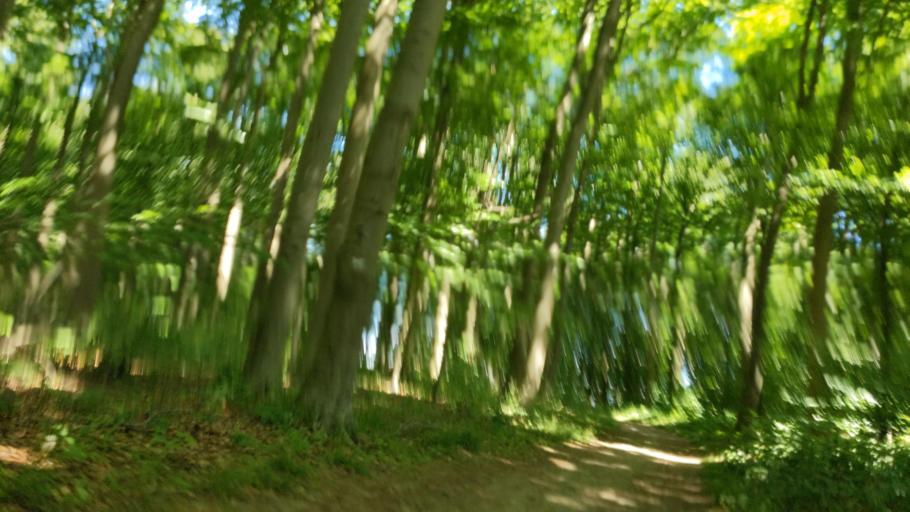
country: DE
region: Schleswig-Holstein
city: Einhaus
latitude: 53.7136
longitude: 10.7391
